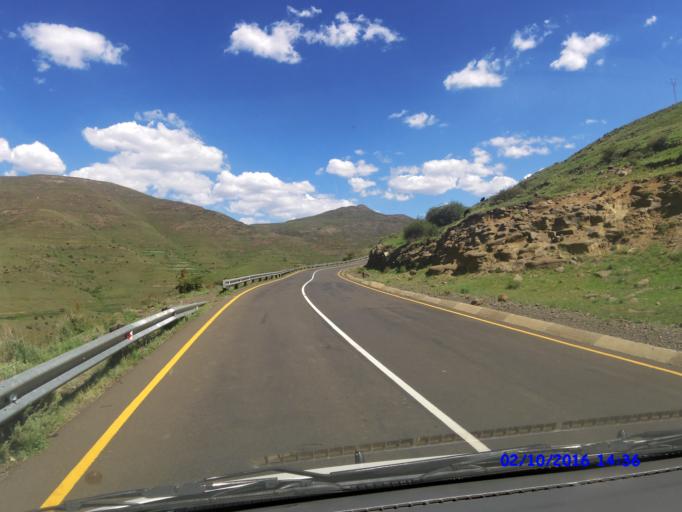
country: LS
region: Maseru
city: Nako
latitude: -29.4959
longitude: 28.0622
